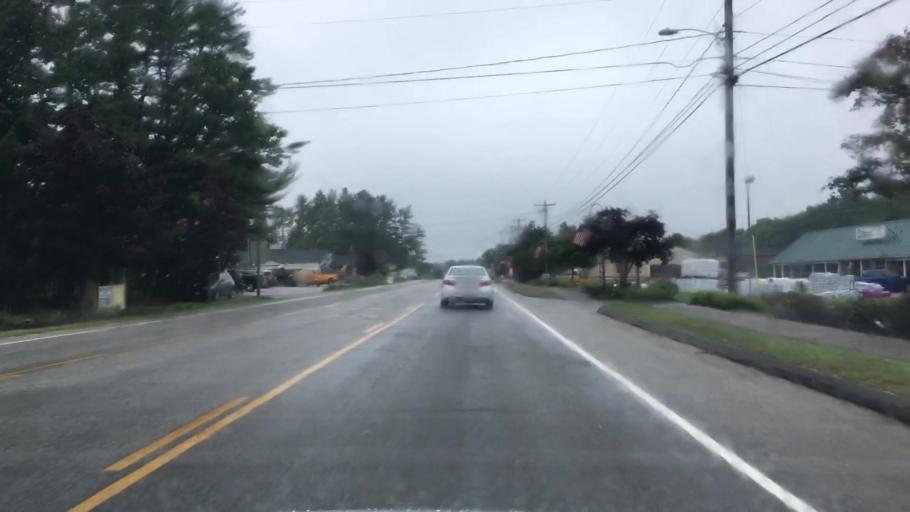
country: US
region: Maine
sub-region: Cumberland County
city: Raymond
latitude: 43.8813
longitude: -70.4656
